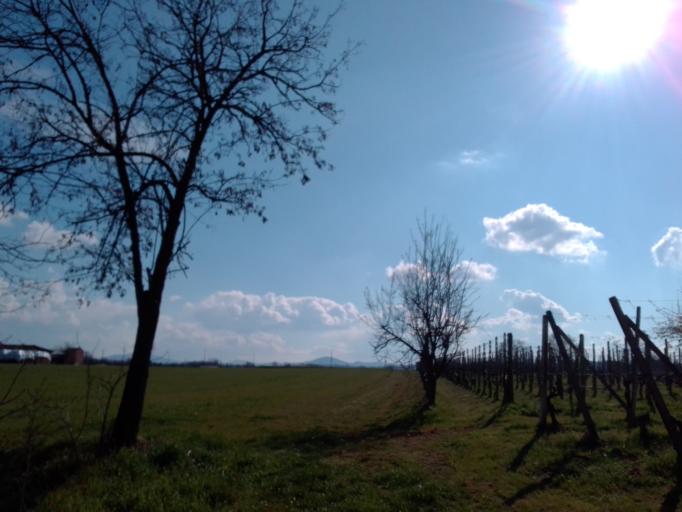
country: IT
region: Emilia-Romagna
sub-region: Provincia di Piacenza
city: Borgonovo Valtidone
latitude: 45.0009
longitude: 9.4312
